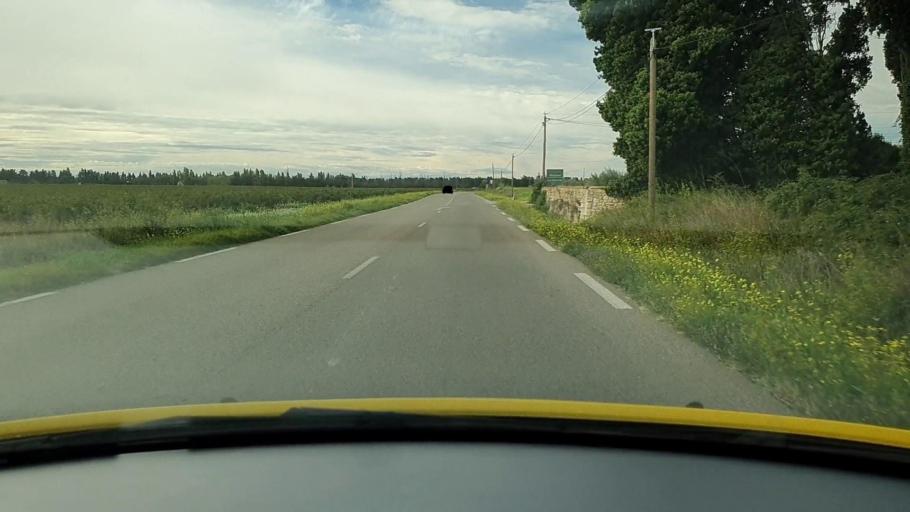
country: FR
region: Languedoc-Roussillon
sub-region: Departement du Gard
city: Jonquieres-Saint-Vincent
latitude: 43.7909
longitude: 4.5818
